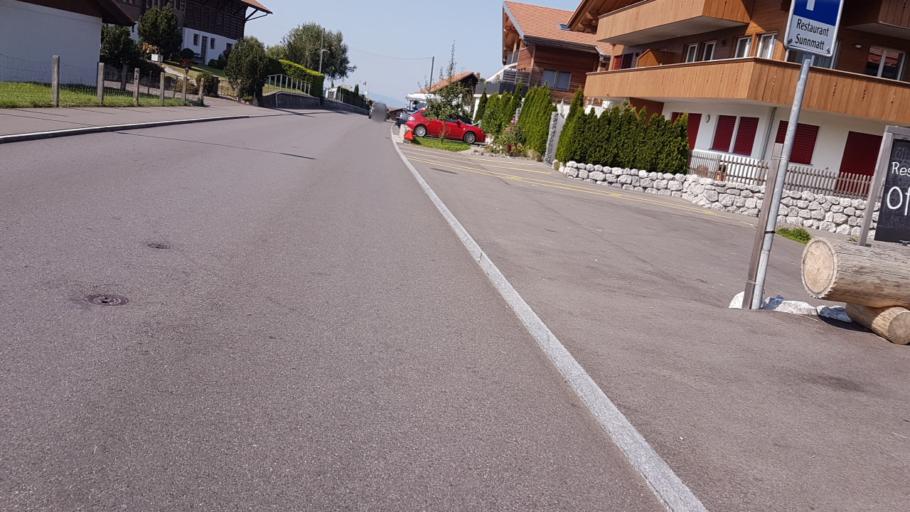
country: CH
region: Bern
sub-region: Frutigen-Niedersimmental District
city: Aeschi
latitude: 46.6524
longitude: 7.7020
